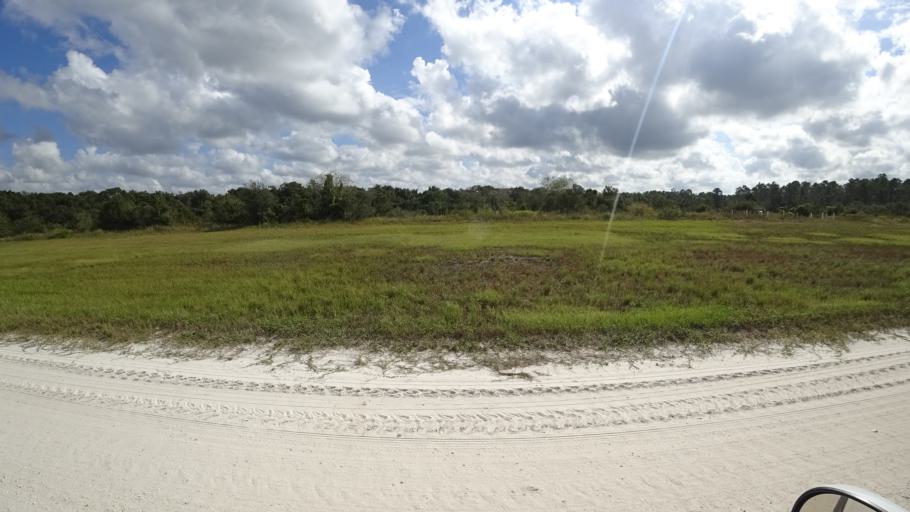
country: US
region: Florida
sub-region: Sarasota County
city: Lake Sarasota
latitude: 27.4225
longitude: -82.1871
